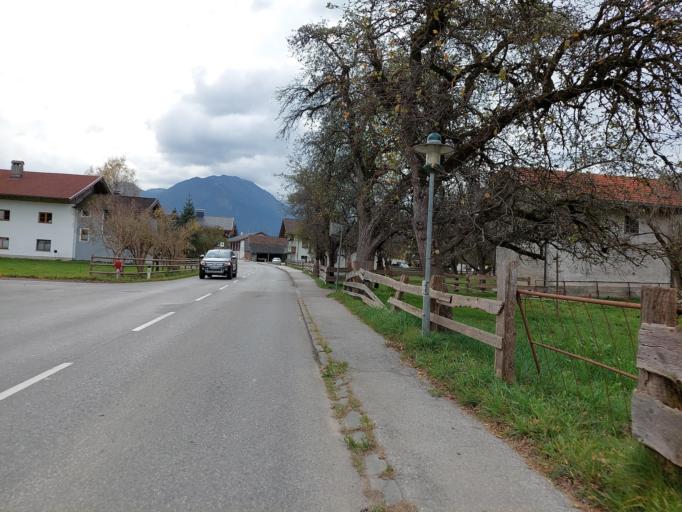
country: AT
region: Tyrol
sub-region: Politischer Bezirk Kufstein
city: Munster
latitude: 47.4268
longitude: 11.8417
